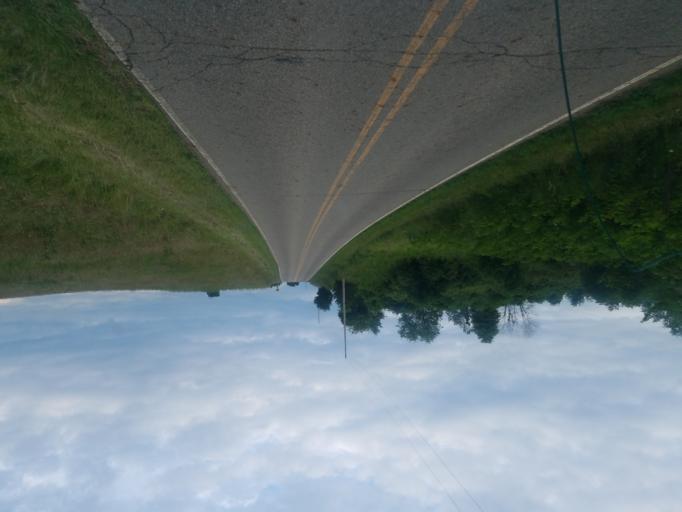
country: US
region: Ohio
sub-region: Knox County
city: Oak Hill
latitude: 40.4173
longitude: -82.1174
